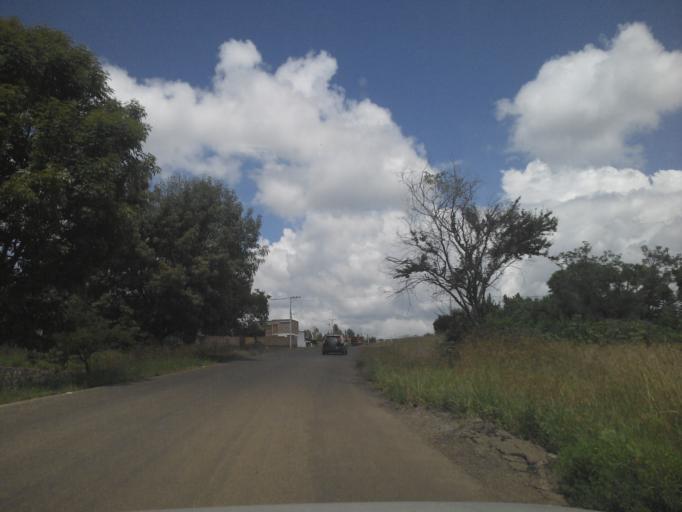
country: MX
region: Jalisco
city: Atotonilco el Alto
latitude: 20.5709
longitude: -102.5018
